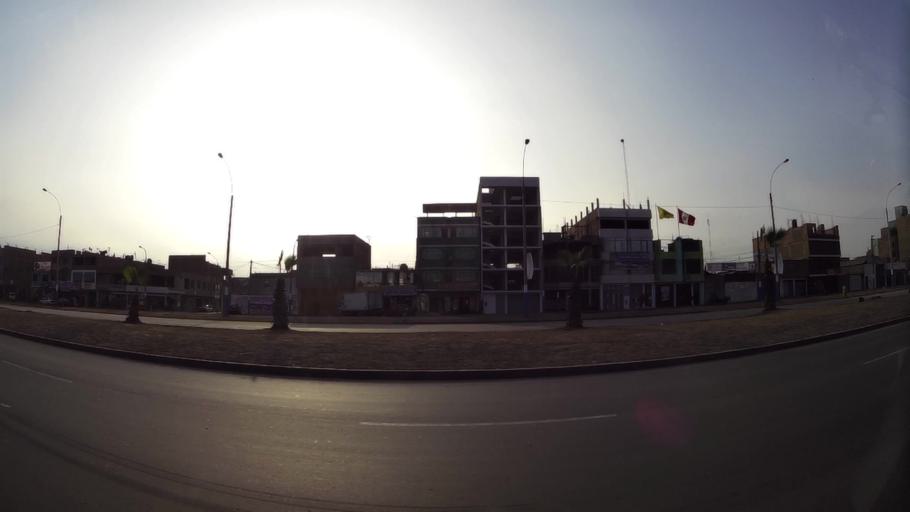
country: PE
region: Lima
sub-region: Lima
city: Independencia
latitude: -11.9788
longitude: -77.0937
